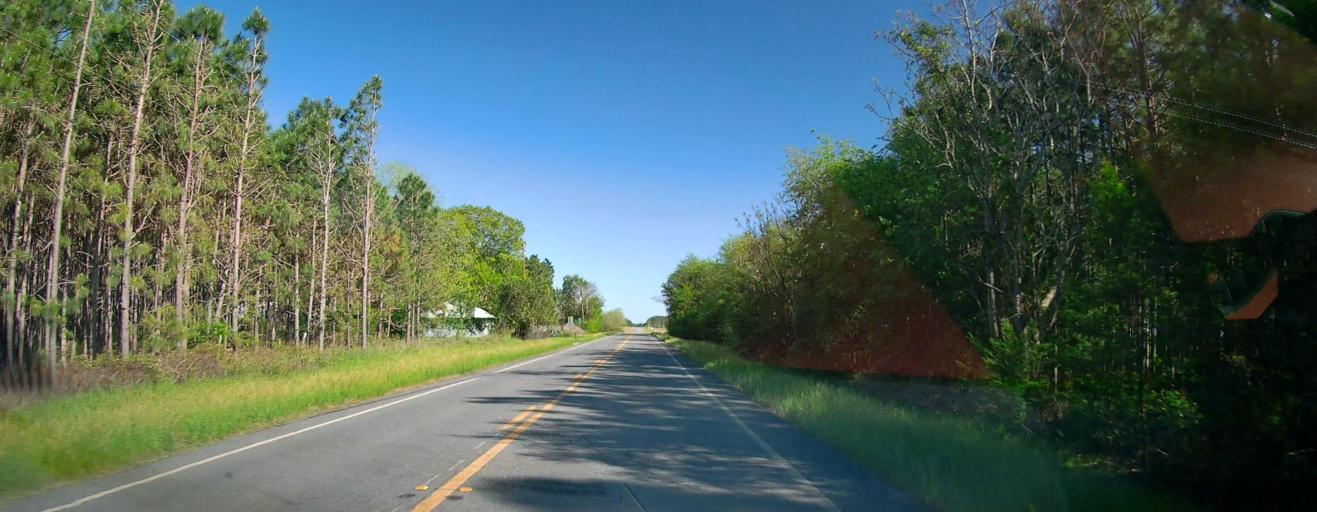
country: US
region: Georgia
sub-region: Wilcox County
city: Rochelle
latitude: 31.9950
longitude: -83.4728
